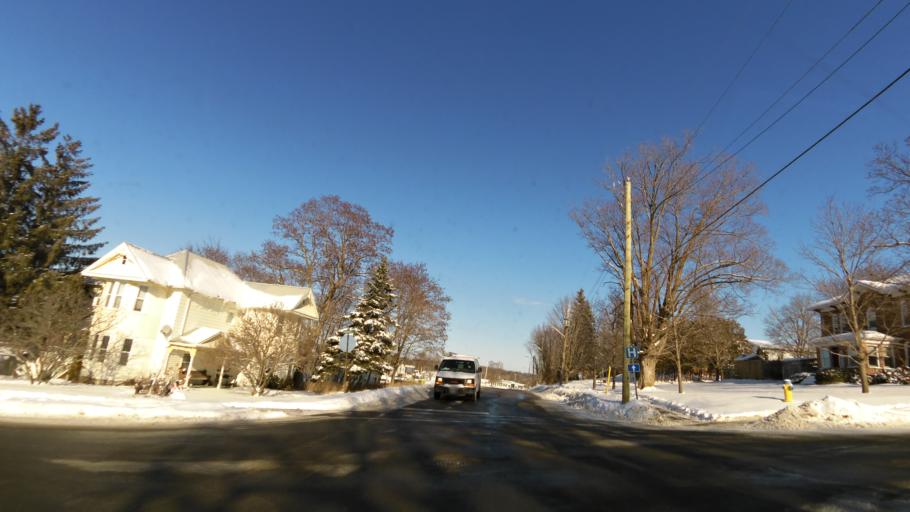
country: CA
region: Ontario
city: Quinte West
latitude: 44.3107
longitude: -77.7922
